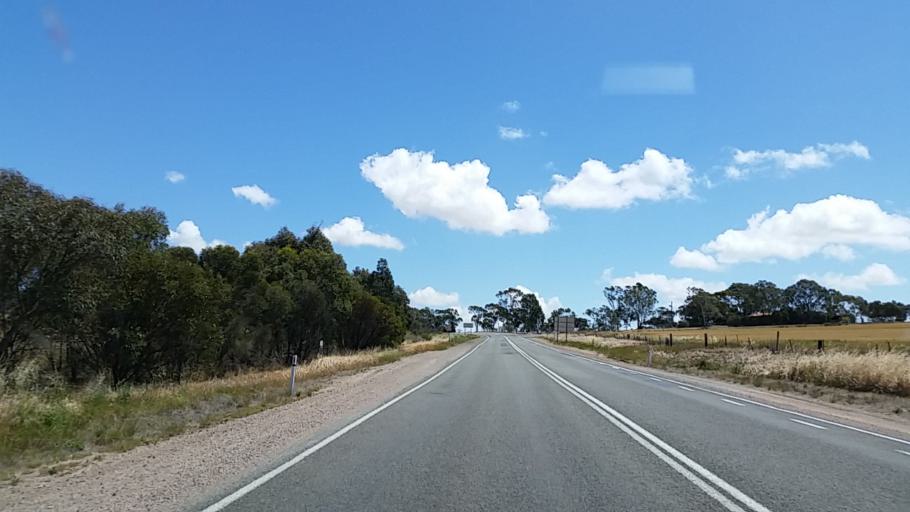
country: AU
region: South Australia
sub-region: Port Pirie City and Dists
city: Crystal Brook
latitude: -33.2830
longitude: 138.2667
